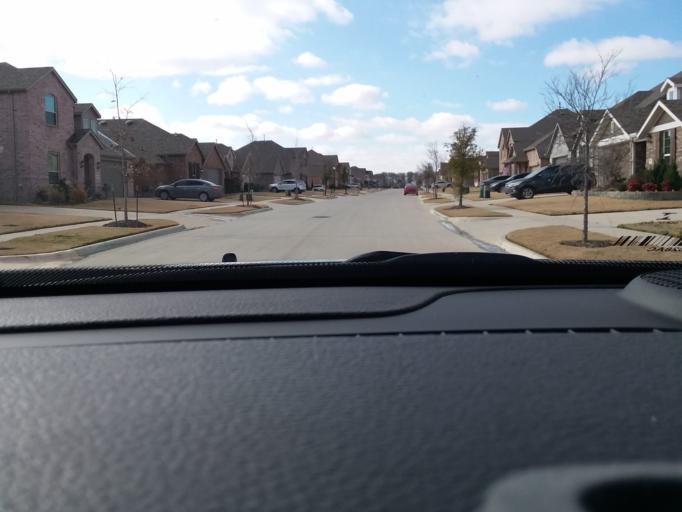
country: US
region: Texas
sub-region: Denton County
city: Little Elm
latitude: 33.2408
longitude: -96.8971
